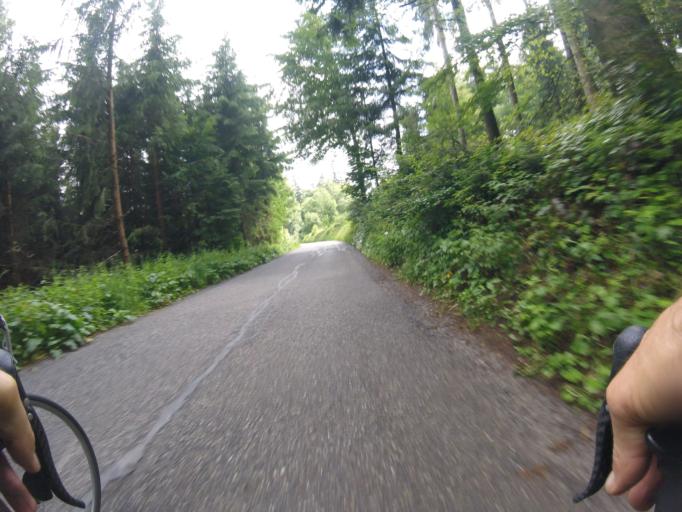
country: CH
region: Bern
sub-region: Bern-Mittelland District
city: Walkringen
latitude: 46.9683
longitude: 7.5977
